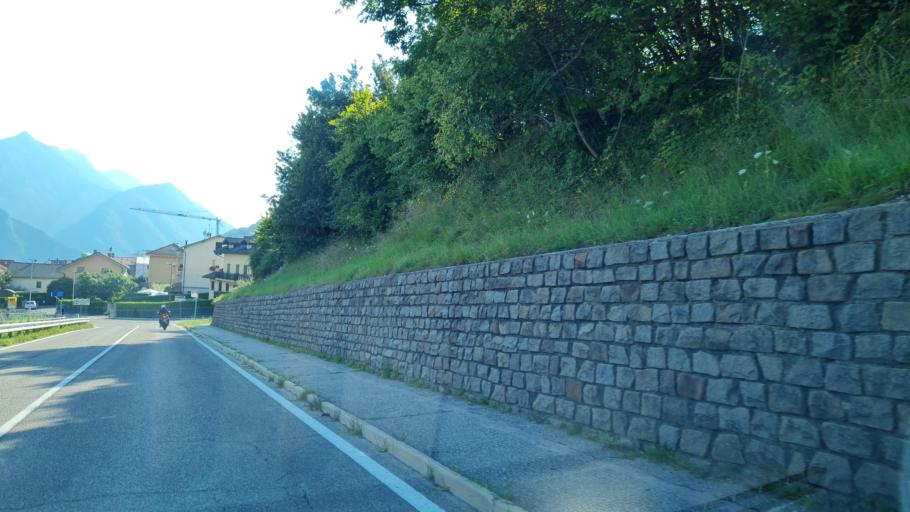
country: IT
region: Trentino-Alto Adige
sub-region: Provincia di Trento
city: Telve
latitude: 46.0710
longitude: 11.4840
